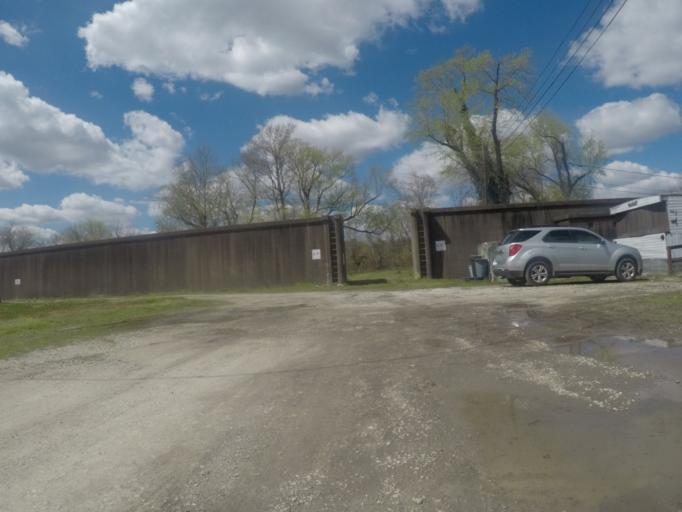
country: US
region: Kentucky
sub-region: Boyd County
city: Catlettsburg
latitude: 38.4016
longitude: -82.5922
